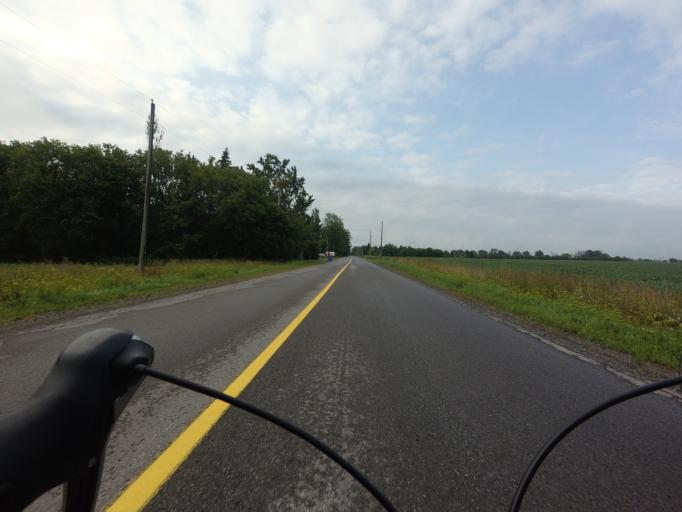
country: CA
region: Ontario
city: Bells Corners
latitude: 45.2454
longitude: -75.8089
